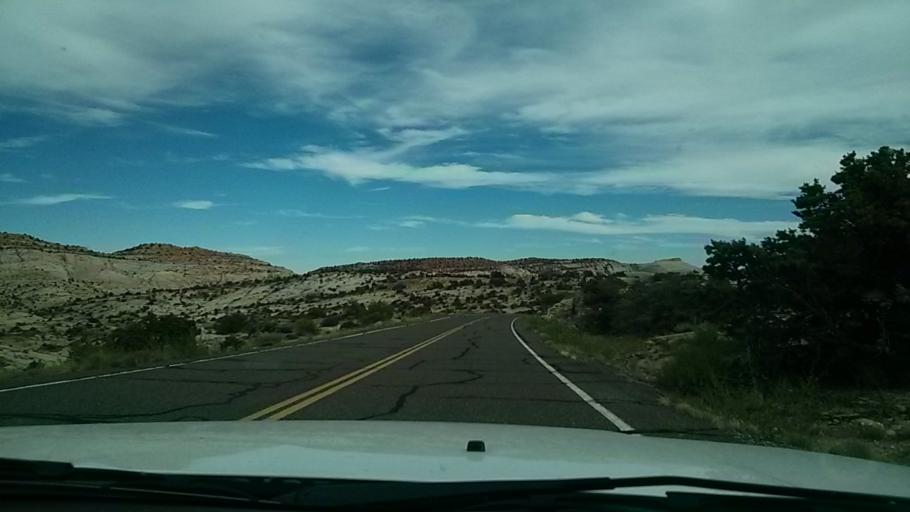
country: US
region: Utah
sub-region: Wayne County
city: Loa
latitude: 37.8110
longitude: -111.4057
